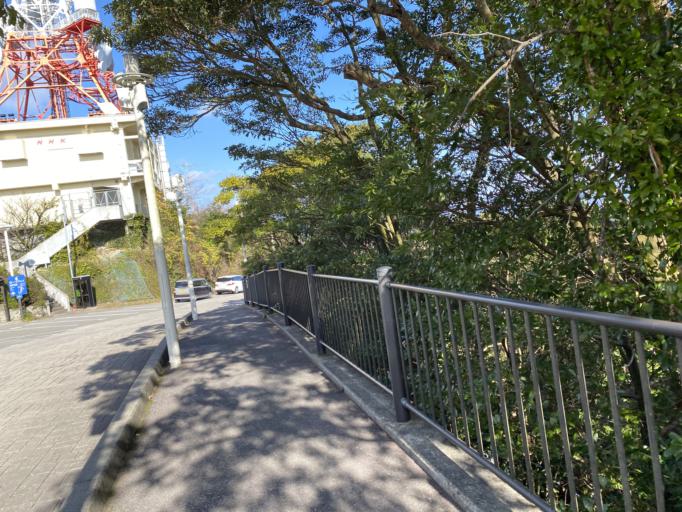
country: JP
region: Nagasaki
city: Nagasaki-shi
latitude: 32.7534
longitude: 129.8495
